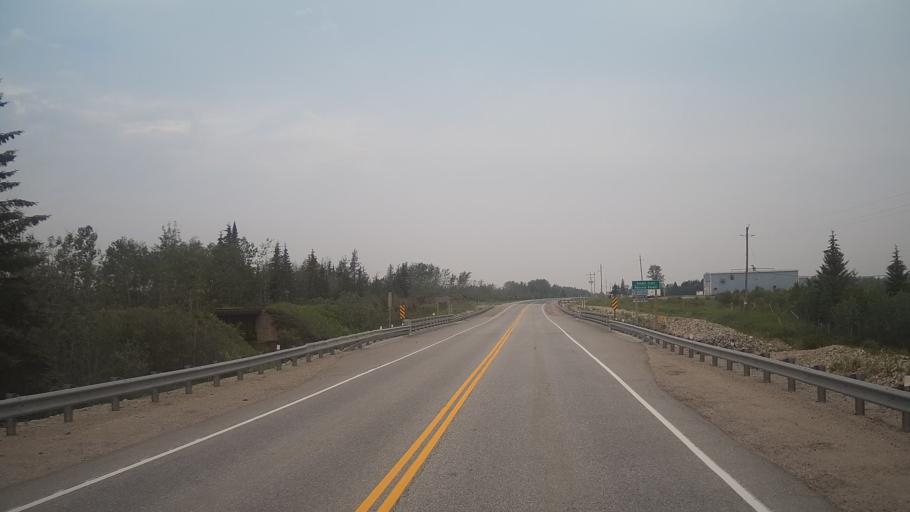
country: CA
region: Ontario
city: Hearst
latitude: 49.6782
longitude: -83.5944
